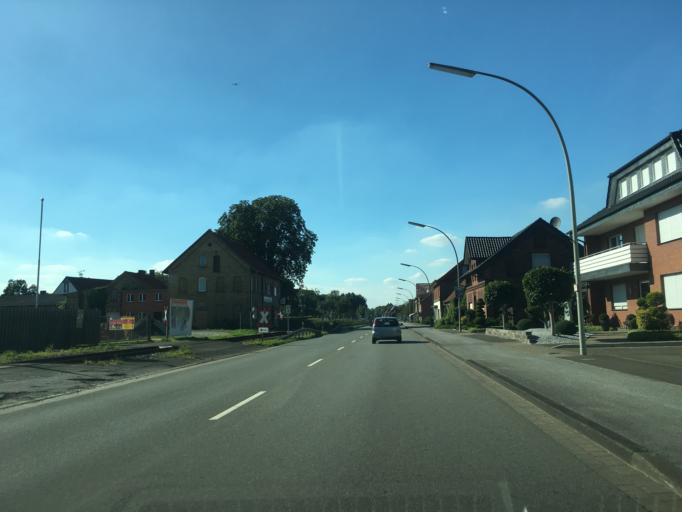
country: DE
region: North Rhine-Westphalia
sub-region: Regierungsbezirk Detmold
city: Harsewinkel
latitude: 51.9008
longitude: 8.1962
